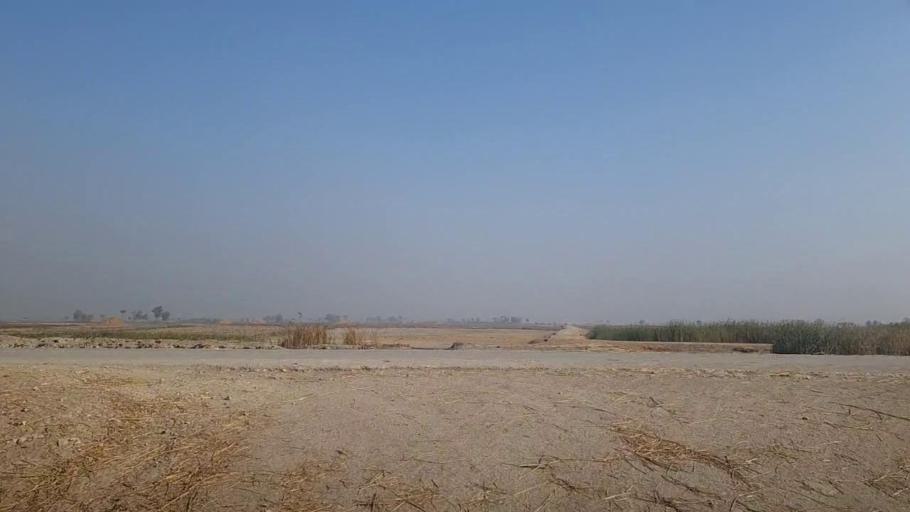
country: PK
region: Sindh
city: Radhan
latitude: 27.1495
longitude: 67.9123
